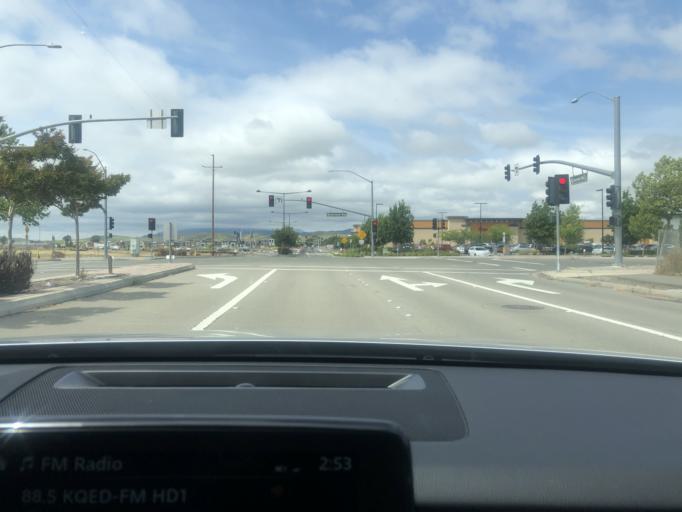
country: US
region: California
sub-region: Alameda County
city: Dublin
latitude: 37.7043
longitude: -121.8933
